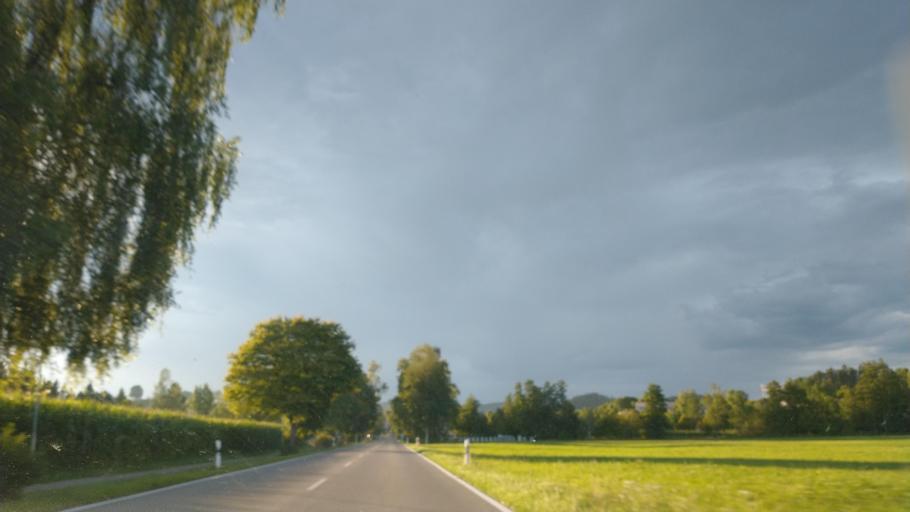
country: DE
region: Baden-Wuerttemberg
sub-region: Tuebingen Region
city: Amtzell
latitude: 47.7007
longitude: 9.7536
